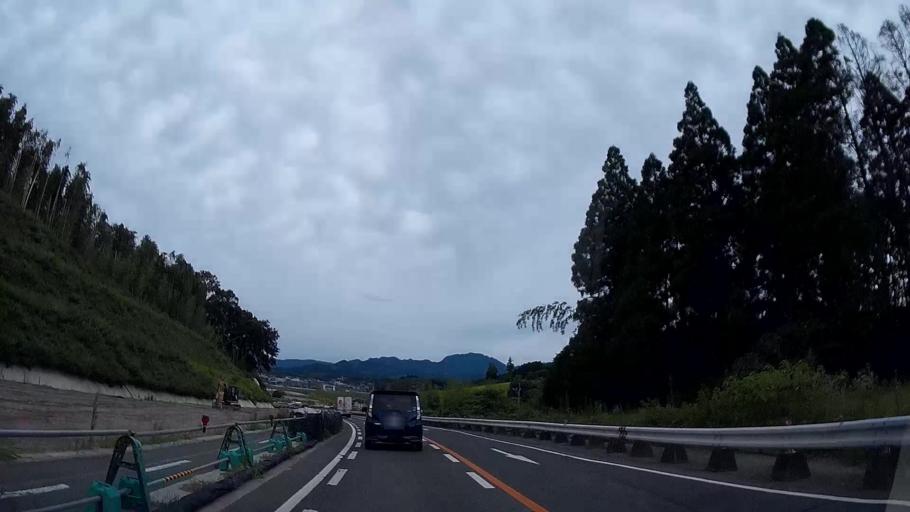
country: JP
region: Kumamoto
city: Kikuchi
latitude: 32.9568
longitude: 130.8219
